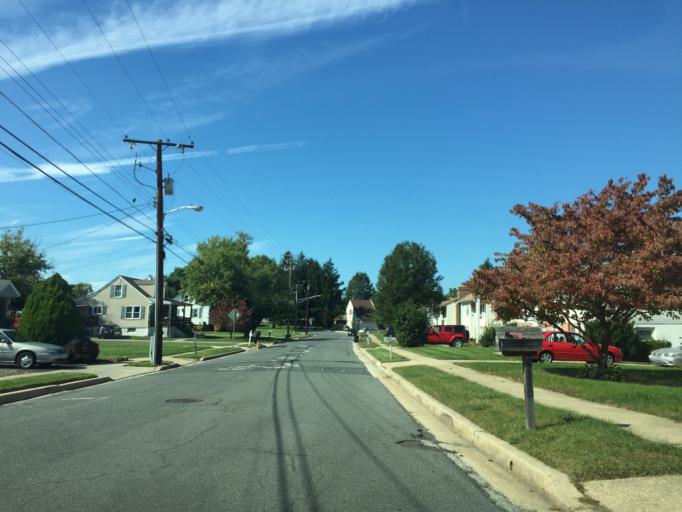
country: US
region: Maryland
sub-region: Baltimore County
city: Perry Hall
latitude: 39.4146
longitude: -76.4674
